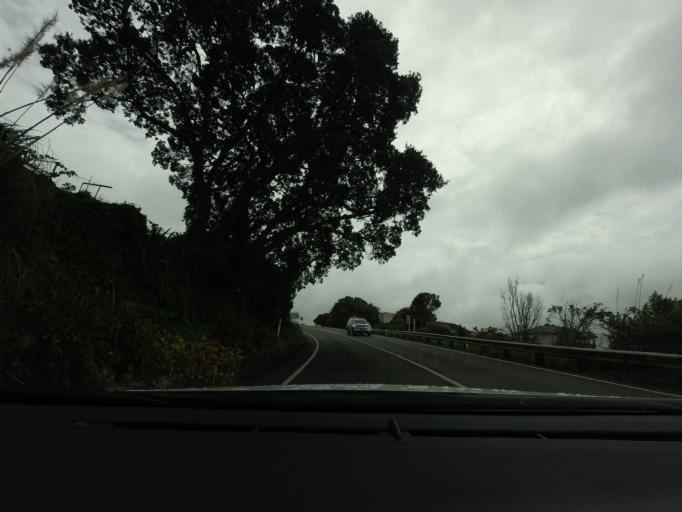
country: NZ
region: Auckland
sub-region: Auckland
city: Rothesay Bay
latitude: -36.5722
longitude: 174.6934
